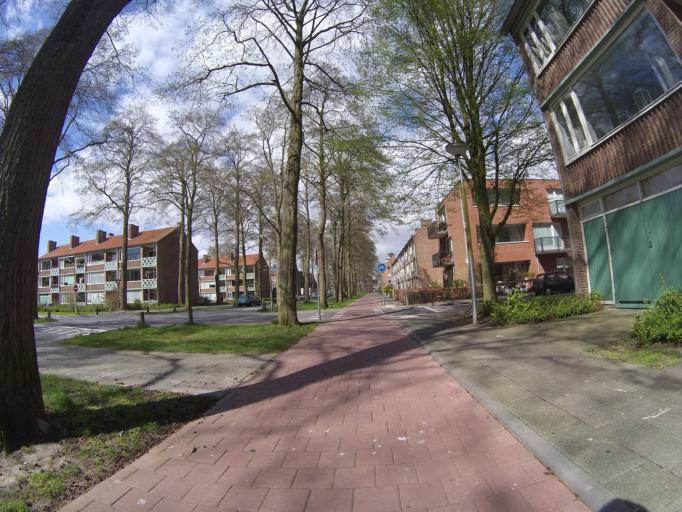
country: NL
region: Utrecht
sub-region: Gemeente Amersfoort
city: Randenbroek
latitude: 52.1503
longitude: 5.4037
